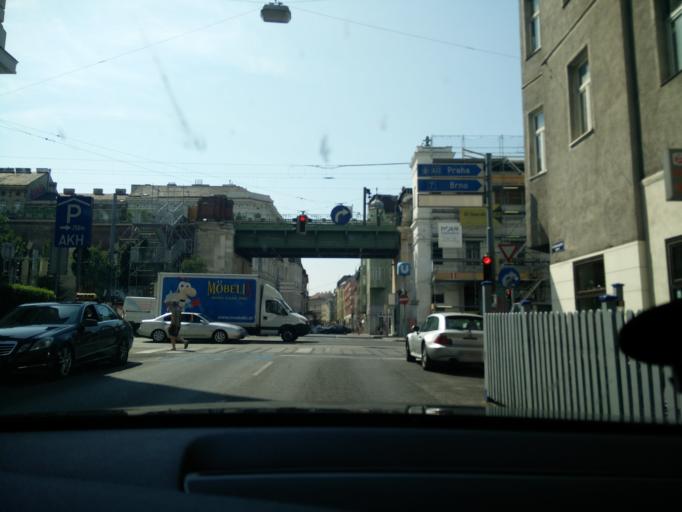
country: AT
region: Vienna
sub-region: Wien Stadt
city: Vienna
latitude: 48.2163
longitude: 16.3424
